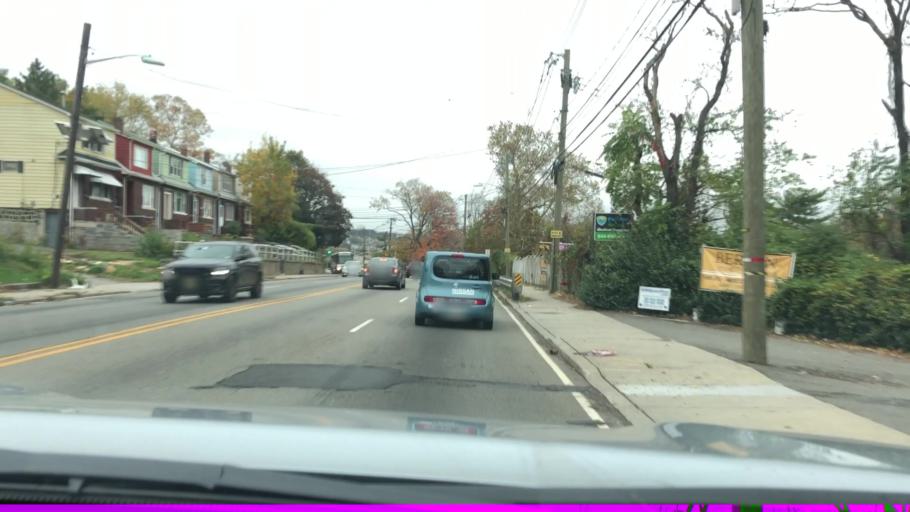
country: US
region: New Jersey
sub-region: Bergen County
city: Ridgefield
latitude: 40.8286
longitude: -74.0104
